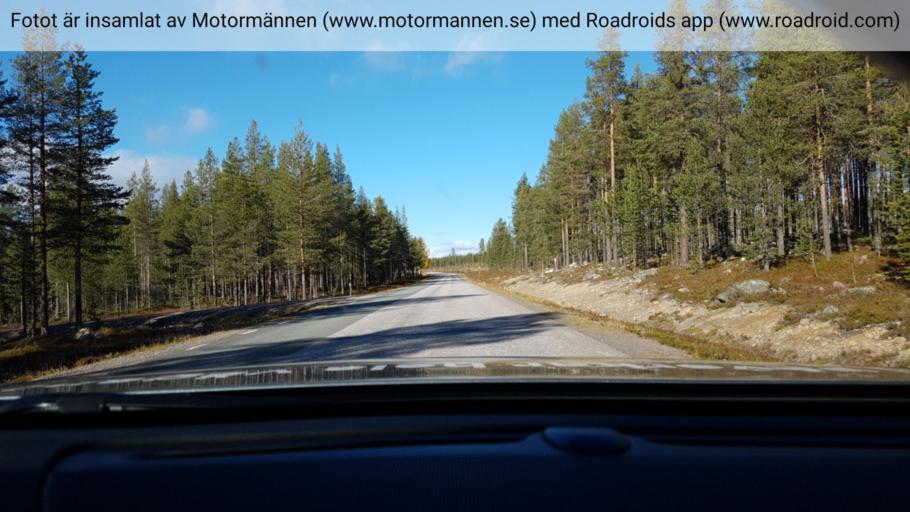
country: SE
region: Vaesterbotten
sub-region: Mala Kommun
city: Mala
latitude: 65.7695
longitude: 18.5376
